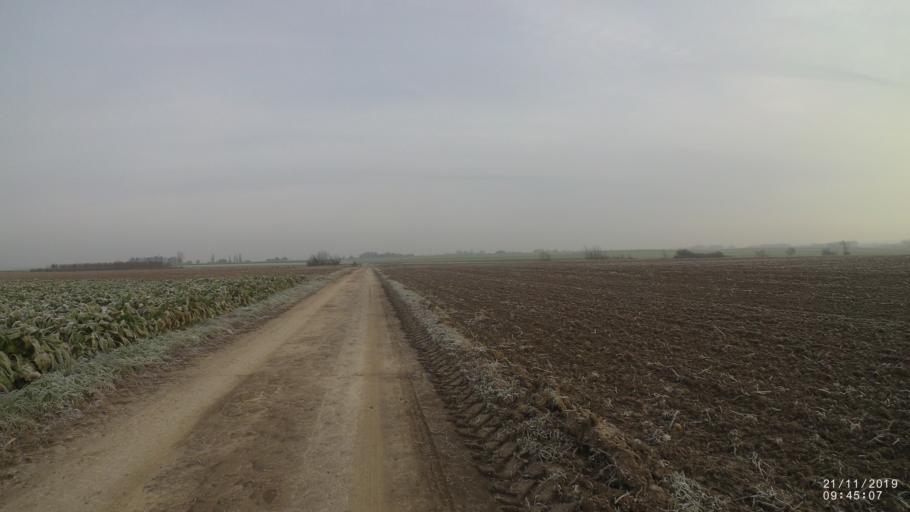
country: BE
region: Flanders
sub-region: Provincie Vlaams-Brabant
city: Tienen
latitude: 50.7886
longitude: 5.0012
